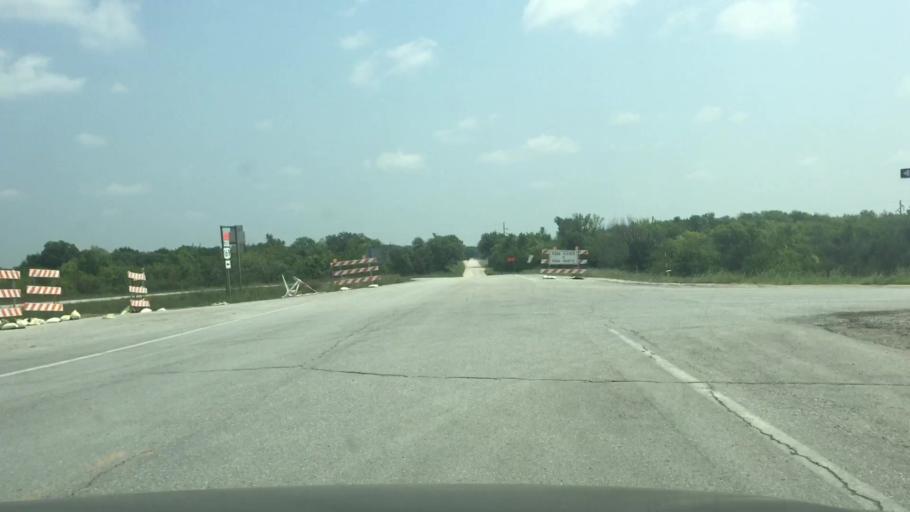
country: US
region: Kansas
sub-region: Allen County
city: Humboldt
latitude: 37.8203
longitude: -95.4091
